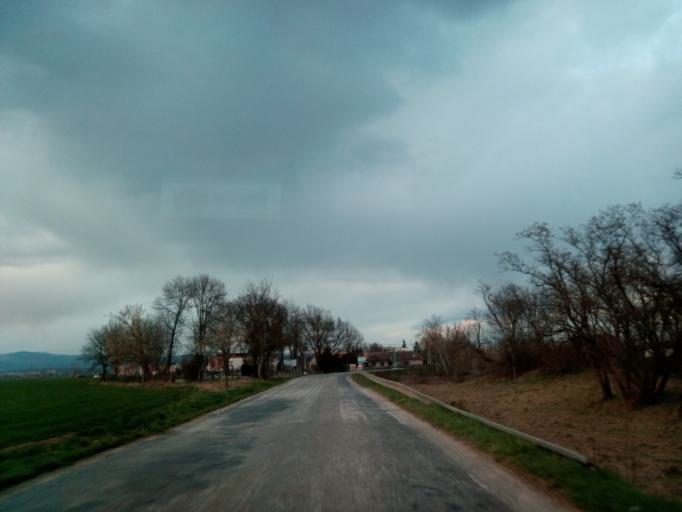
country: SK
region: Kosicky
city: Moldava nad Bodvou
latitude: 48.5851
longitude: 20.9862
